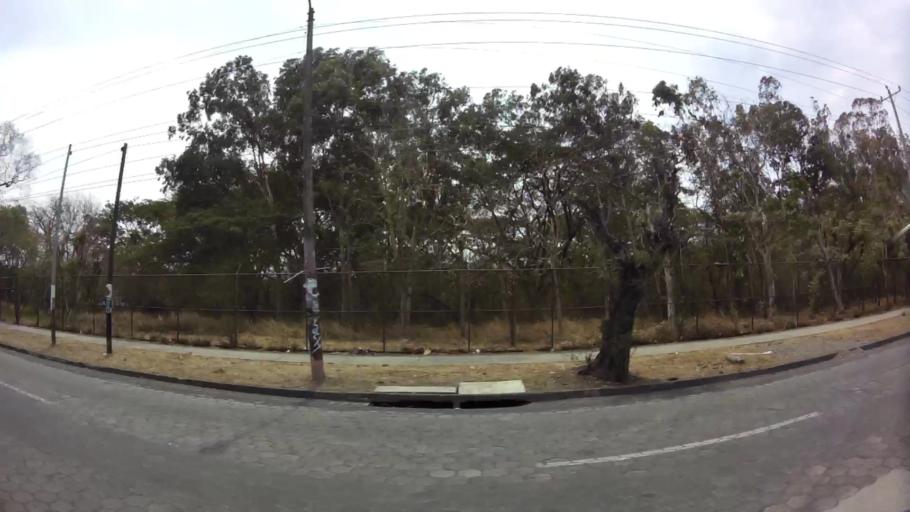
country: NI
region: Managua
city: Ciudad Sandino
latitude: 12.1421
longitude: -86.3062
